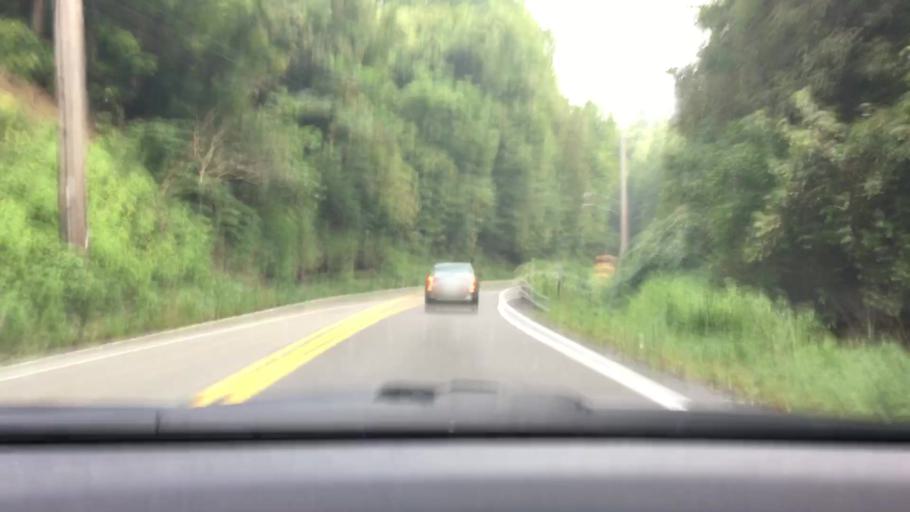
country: US
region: Pennsylvania
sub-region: Allegheny County
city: West Homestead
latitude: 40.3750
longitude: -79.9206
